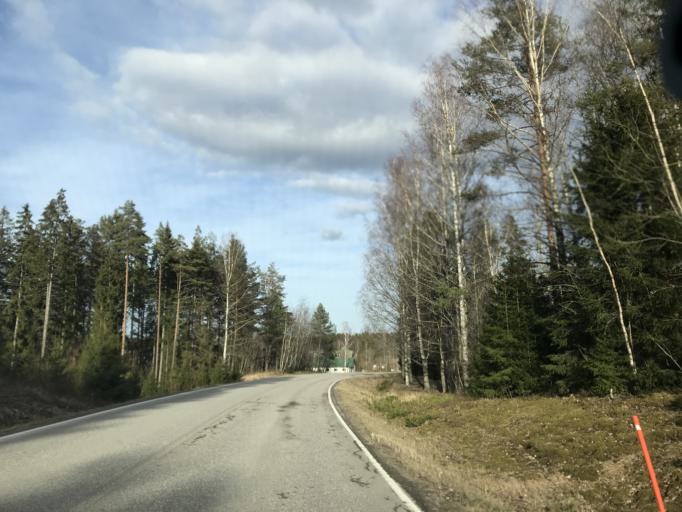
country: FI
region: Uusimaa
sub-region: Raaseporin
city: Ekenaes
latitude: 60.0819
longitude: 23.3594
